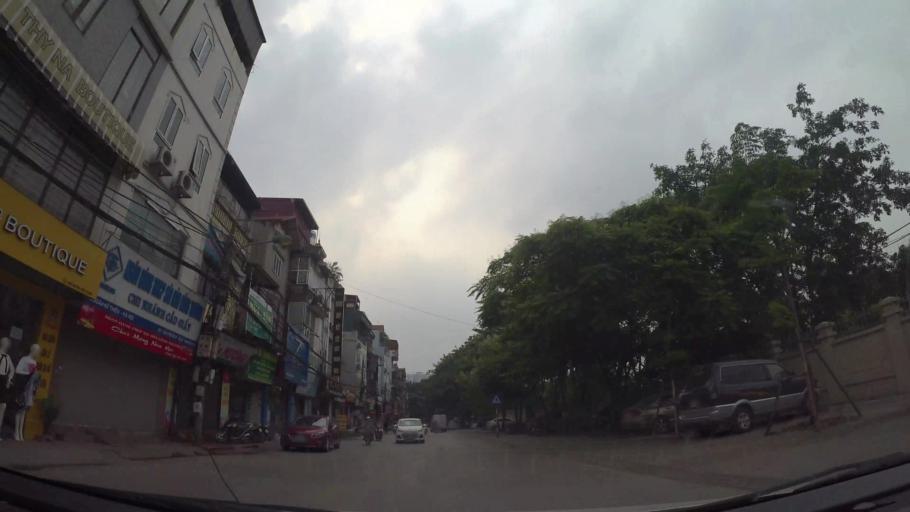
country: VN
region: Ha Noi
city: Cau Dien
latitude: 21.0411
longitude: 105.7787
